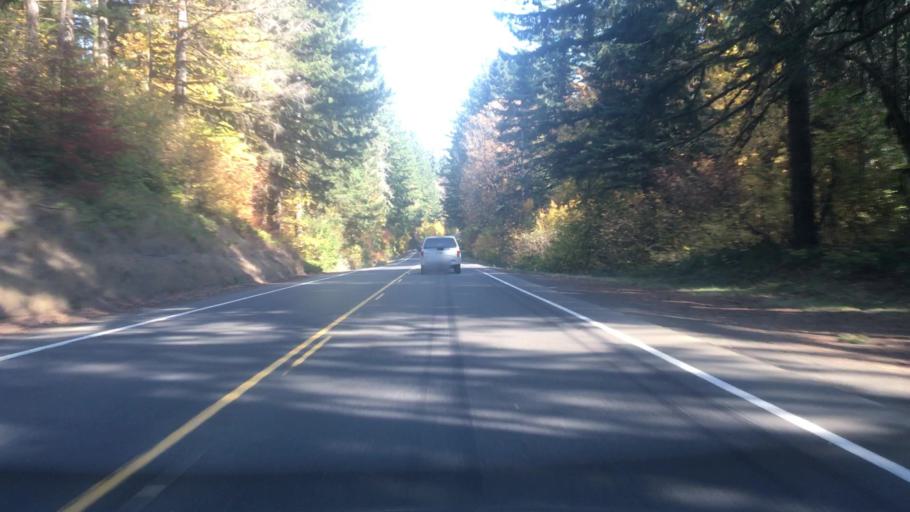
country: US
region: Oregon
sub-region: Polk County
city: Grand Ronde
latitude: 45.0602
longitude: -123.6716
